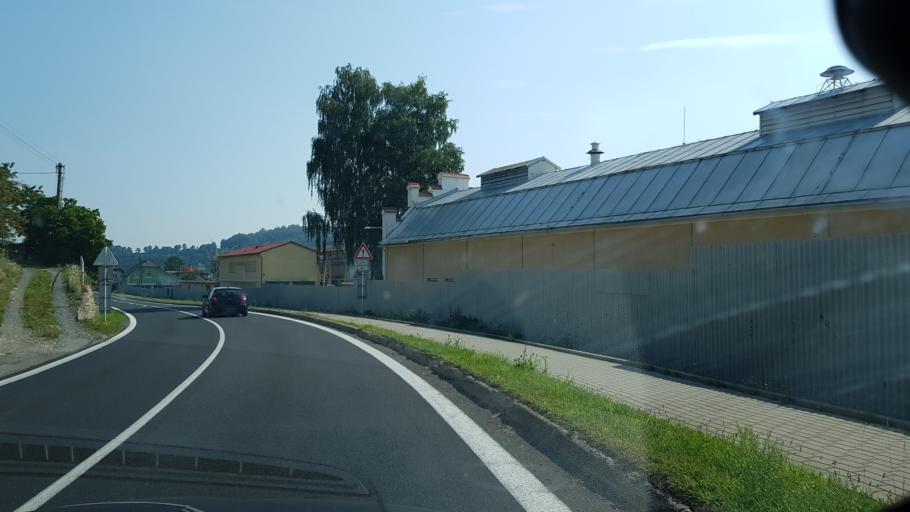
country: CZ
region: Olomoucky
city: Ceska Ves
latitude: 50.2576
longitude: 17.2289
